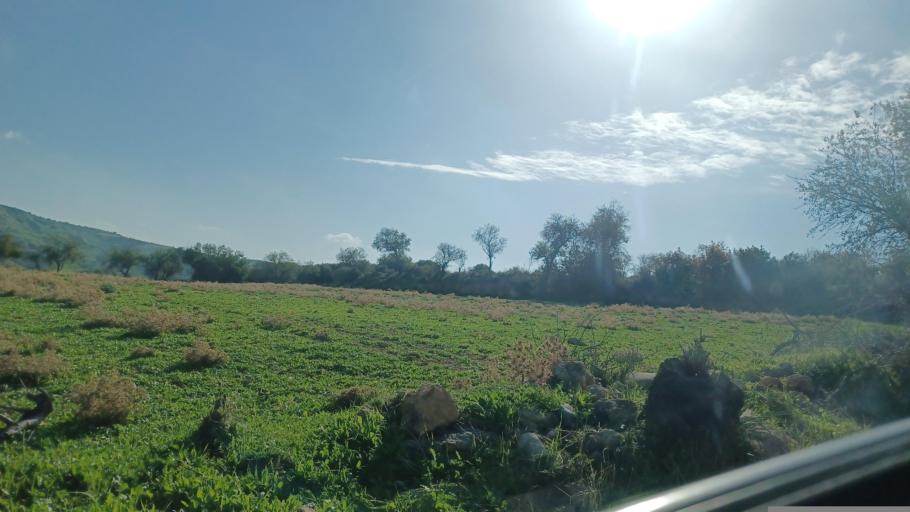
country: CY
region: Pafos
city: Mesogi
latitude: 34.7640
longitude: 32.5757
